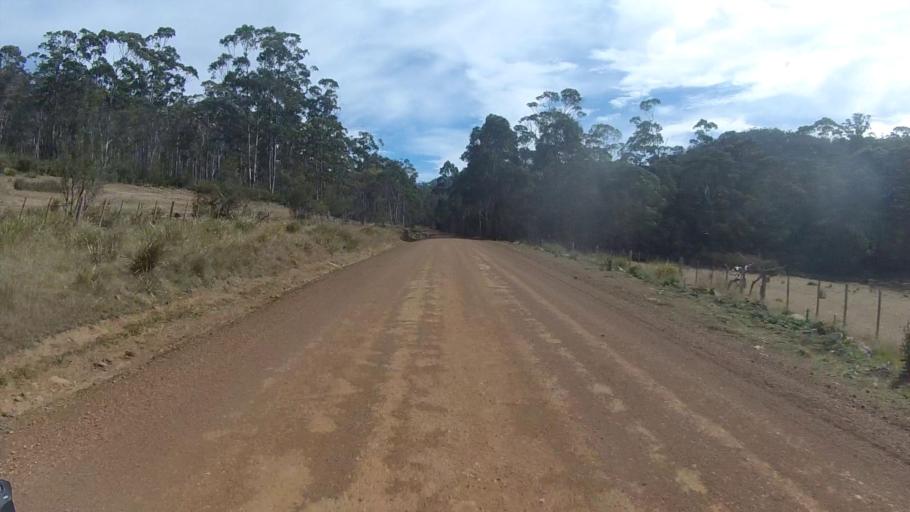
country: AU
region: Tasmania
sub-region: Sorell
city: Sorell
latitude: -42.6301
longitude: 147.9018
